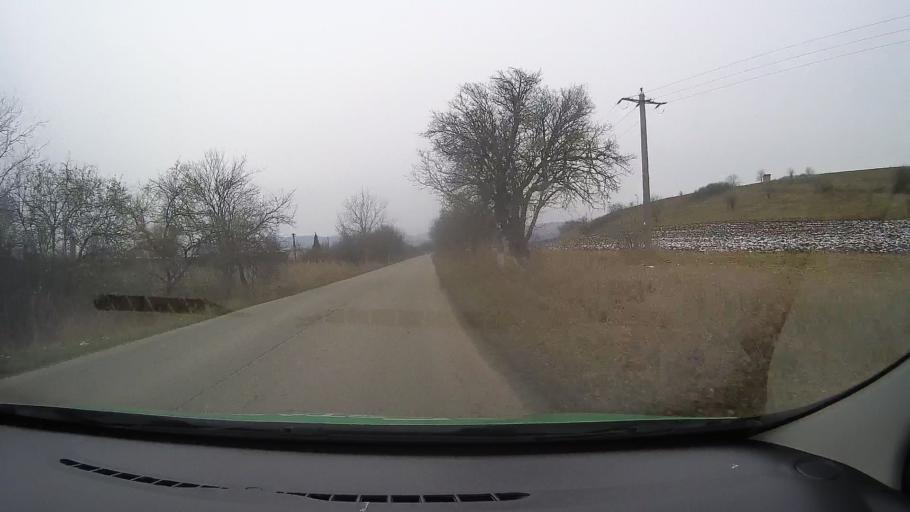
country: RO
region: Hunedoara
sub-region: Comuna Romos
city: Romos
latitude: 45.8785
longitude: 23.2599
